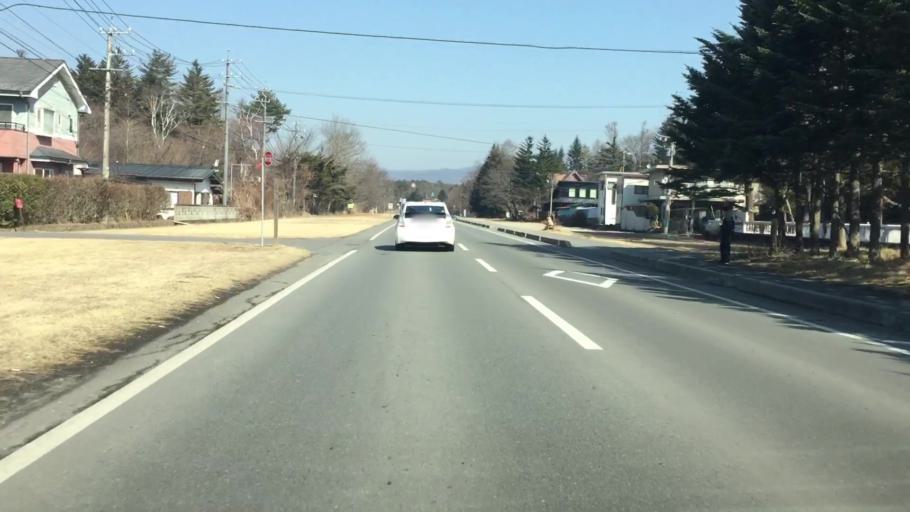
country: JP
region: Nagano
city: Saku
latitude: 36.3145
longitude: 138.6312
